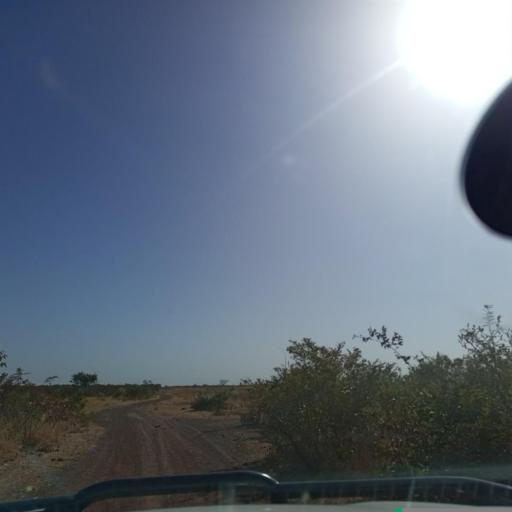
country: ML
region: Koulikoro
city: Koulikoro
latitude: 12.6917
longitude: -7.3655
